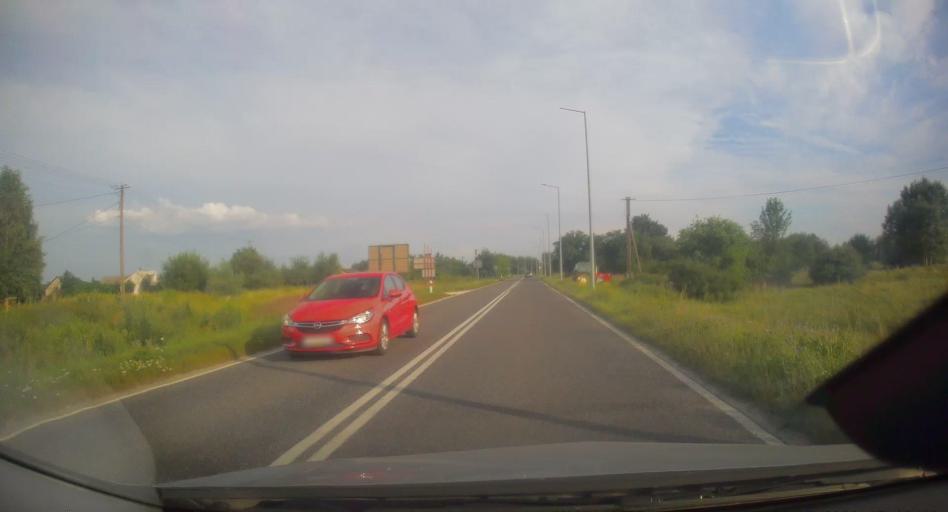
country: PL
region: Lesser Poland Voivodeship
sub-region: Powiat brzeski
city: Szczurowa
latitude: 50.1588
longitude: 20.6033
